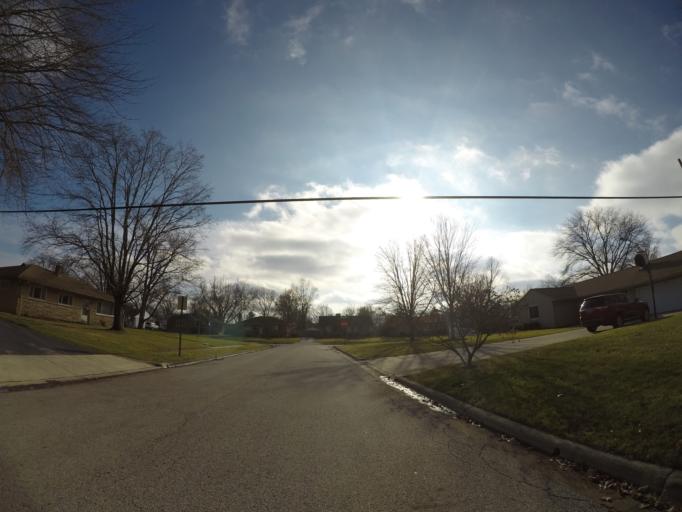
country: US
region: Ohio
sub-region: Franklin County
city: Upper Arlington
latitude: 40.0233
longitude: -83.0667
